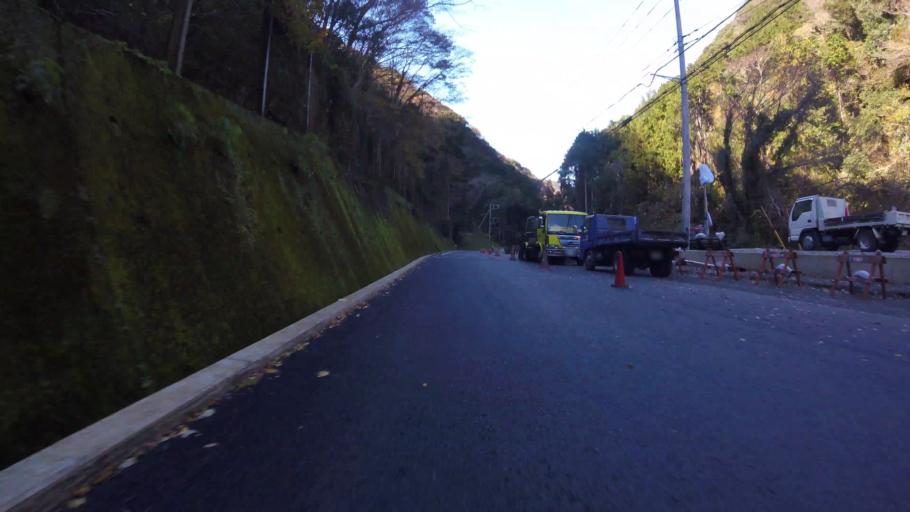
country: JP
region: Shizuoka
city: Shimoda
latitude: 34.7449
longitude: 138.8410
